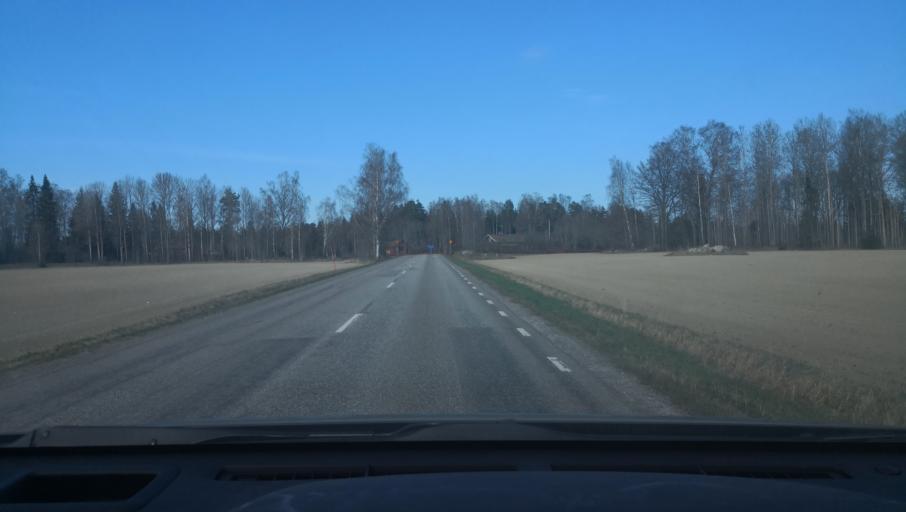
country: SE
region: Uppsala
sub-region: Heby Kommun
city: Heby
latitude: 59.9630
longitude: 16.8909
